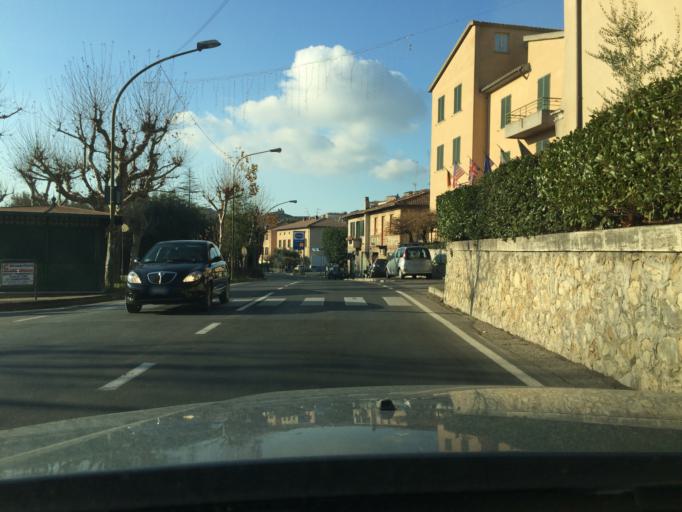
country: IT
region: Umbria
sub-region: Provincia di Terni
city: Amelia
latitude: 42.5540
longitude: 12.4209
